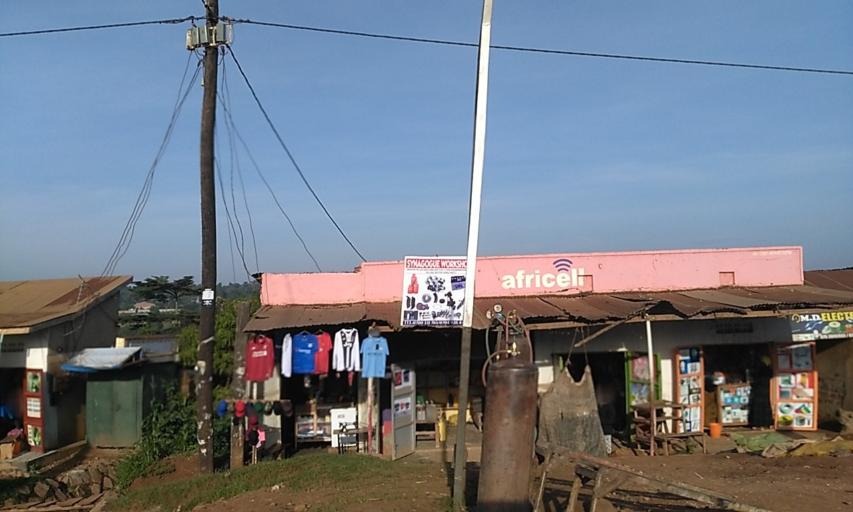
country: UG
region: Central Region
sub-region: Wakiso District
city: Kireka
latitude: 0.4204
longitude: 32.5974
